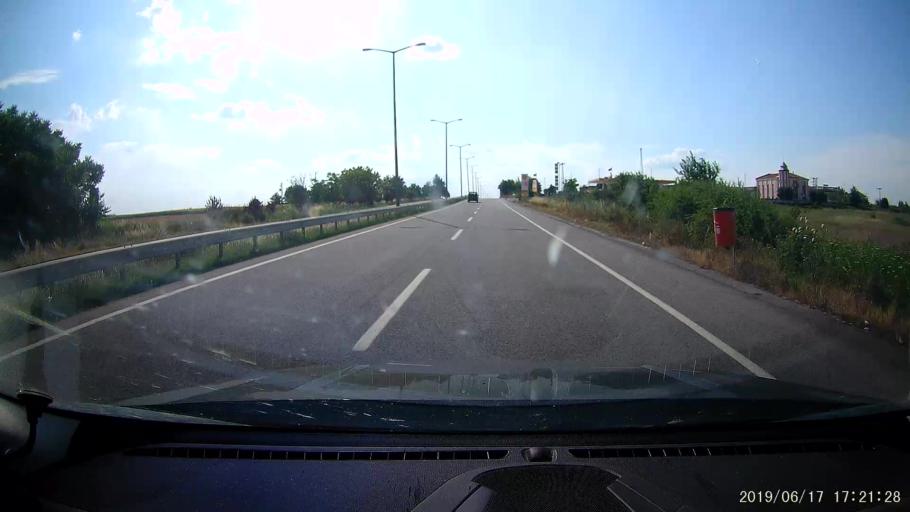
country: GR
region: East Macedonia and Thrace
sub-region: Nomos Evrou
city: Rizia
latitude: 41.7062
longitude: 26.3937
